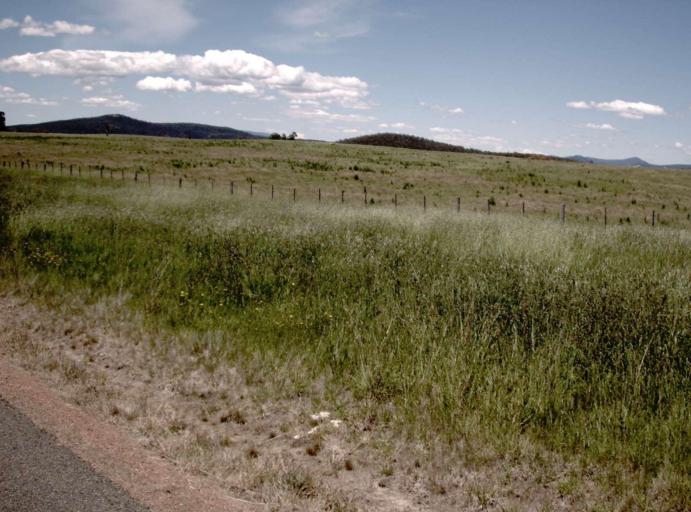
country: AU
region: New South Wales
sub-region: Snowy River
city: Jindabyne
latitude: -37.0884
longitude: 148.2702
